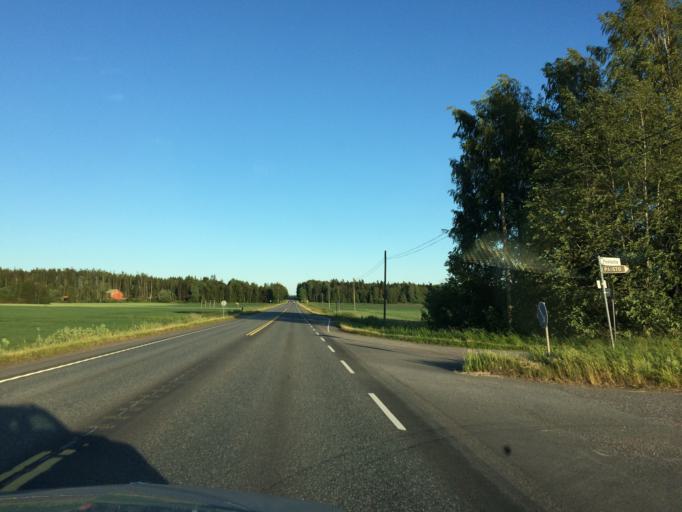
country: FI
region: Haeme
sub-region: Haemeenlinna
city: Tervakoski
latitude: 60.7983
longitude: 24.6645
